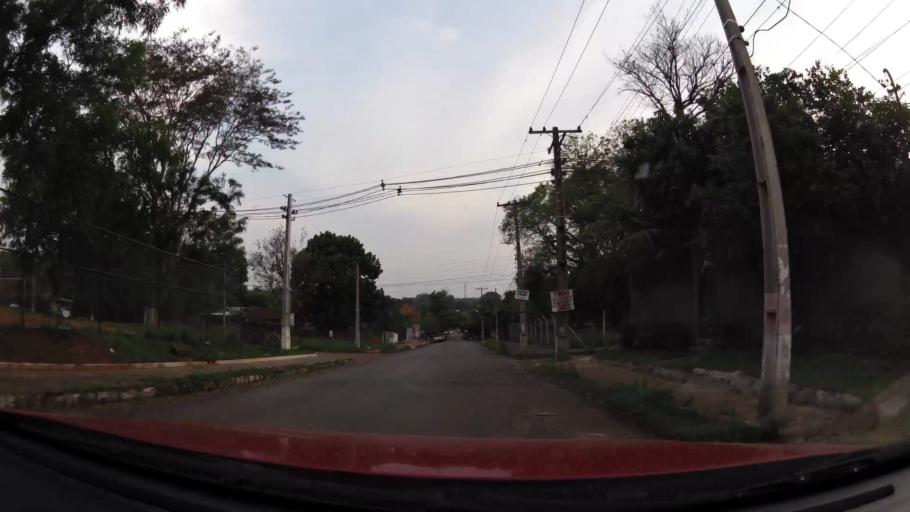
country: PY
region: Central
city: Lambare
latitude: -25.3395
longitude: -57.6159
